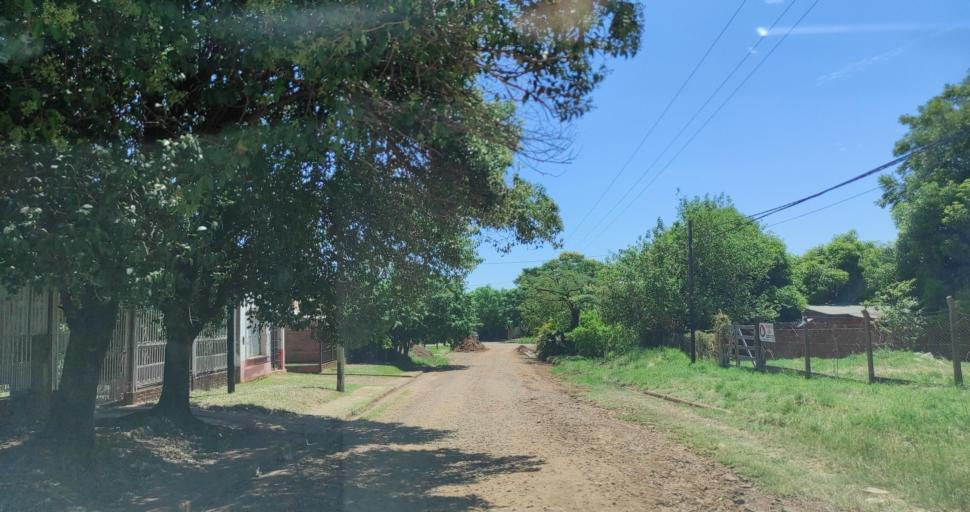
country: AR
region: Misiones
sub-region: Departamento de Capital
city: Posadas
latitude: -27.4265
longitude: -55.8926
